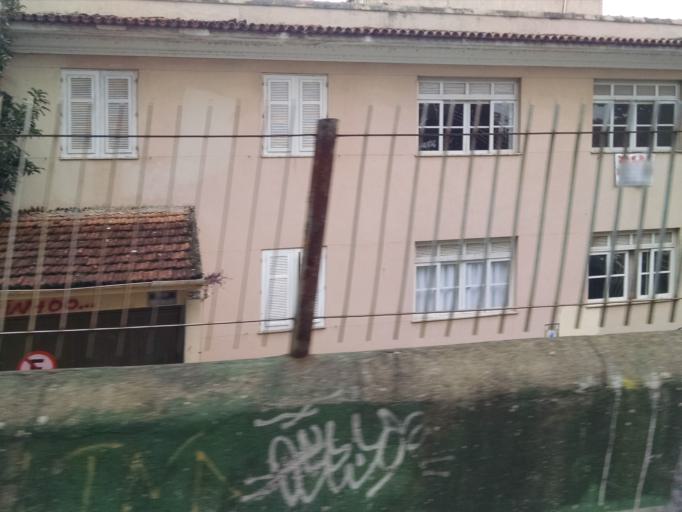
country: BR
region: Rio de Janeiro
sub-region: Rio De Janeiro
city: Rio de Janeiro
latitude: -22.9202
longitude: -43.1848
